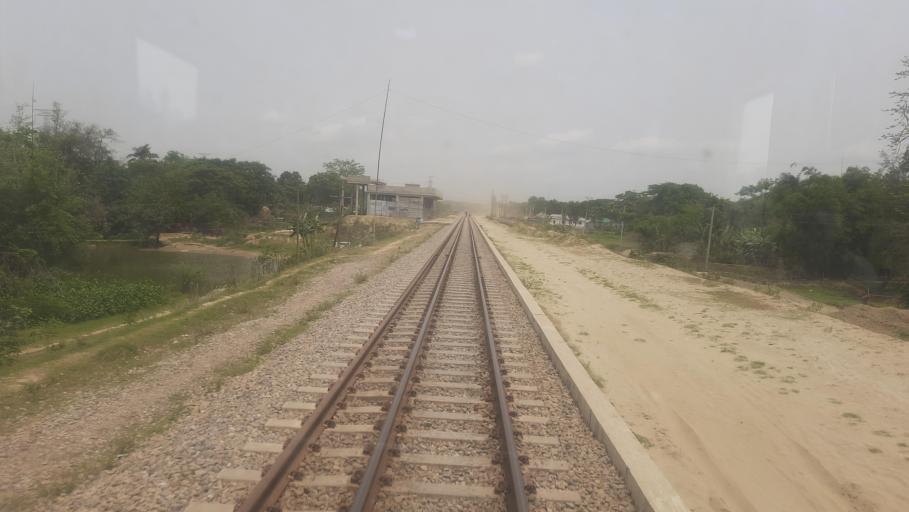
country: IN
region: Tripura
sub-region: West Tripura
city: Barjala
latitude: 23.6685
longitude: 91.1550
